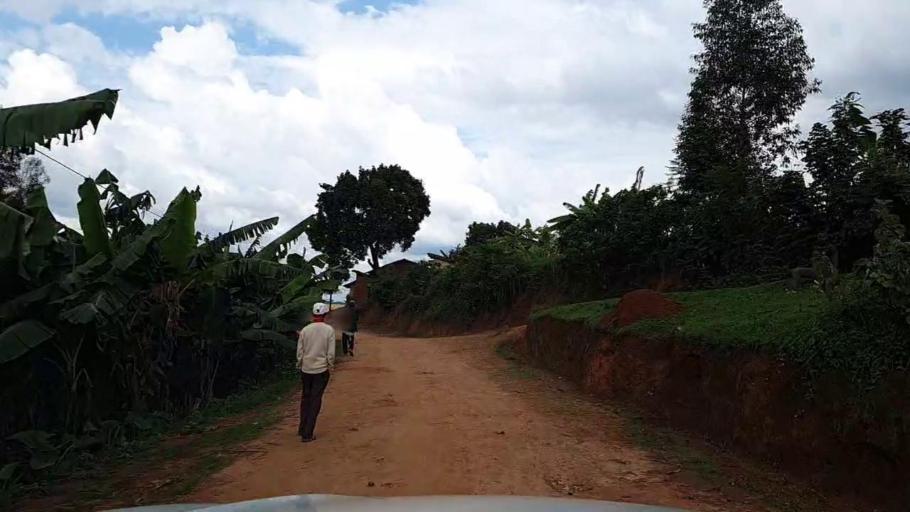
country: RW
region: Southern Province
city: Gikongoro
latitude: -2.4220
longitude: 29.6488
